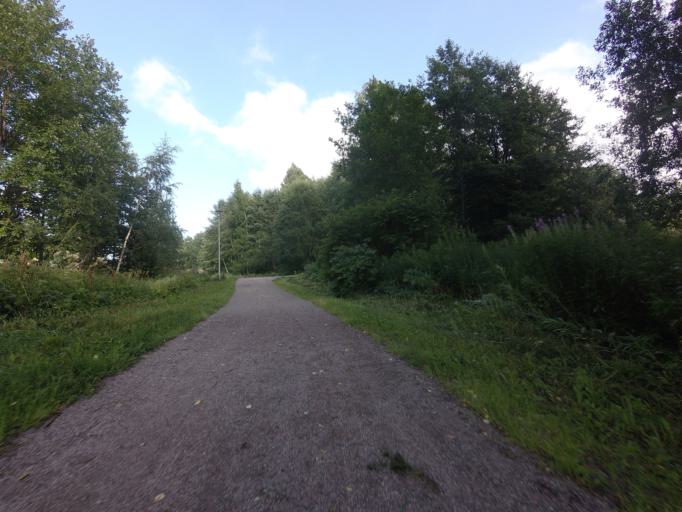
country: FI
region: Uusimaa
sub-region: Helsinki
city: Espoo
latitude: 60.1711
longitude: 24.6772
